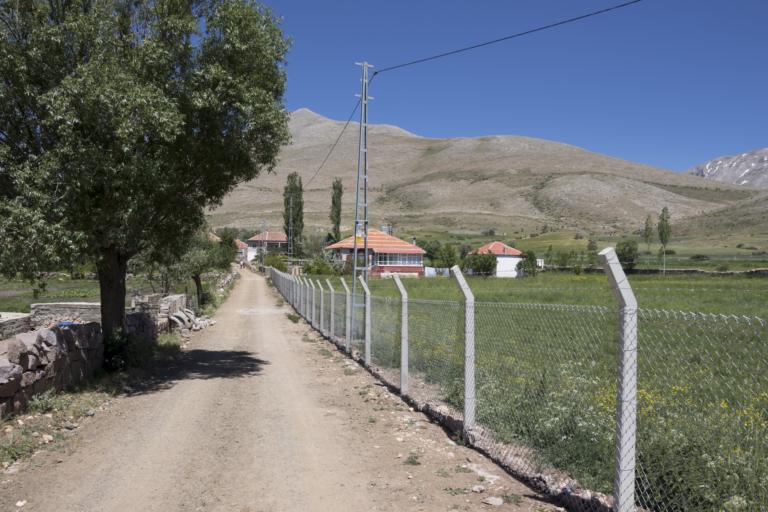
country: TR
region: Kayseri
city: Toklar
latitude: 38.4197
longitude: 36.0973
